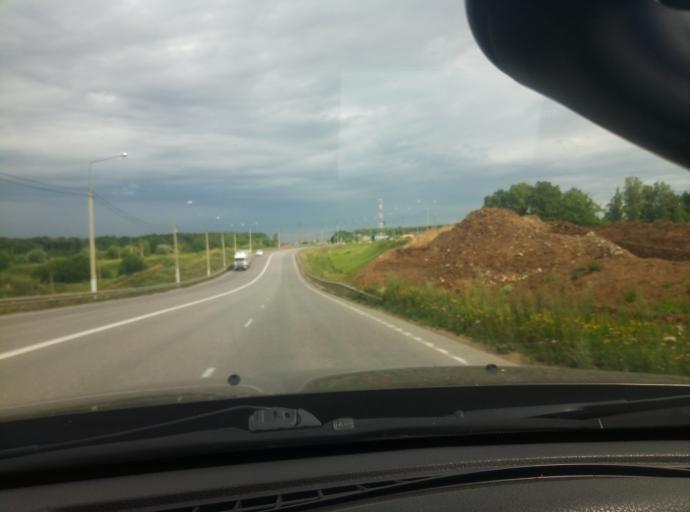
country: RU
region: Tula
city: Novogurovskiy
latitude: 54.4590
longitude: 37.5093
